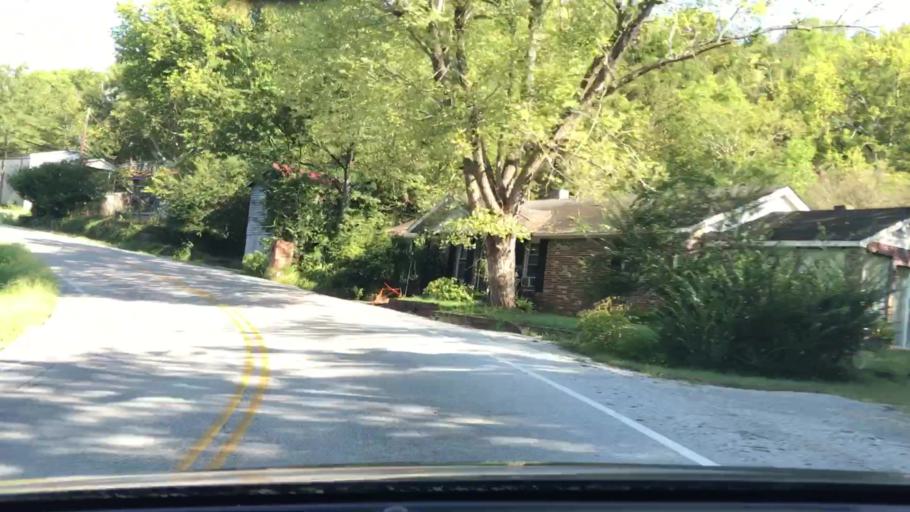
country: US
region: Tennessee
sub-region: Smith County
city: Carthage
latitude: 36.2675
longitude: -85.9553
